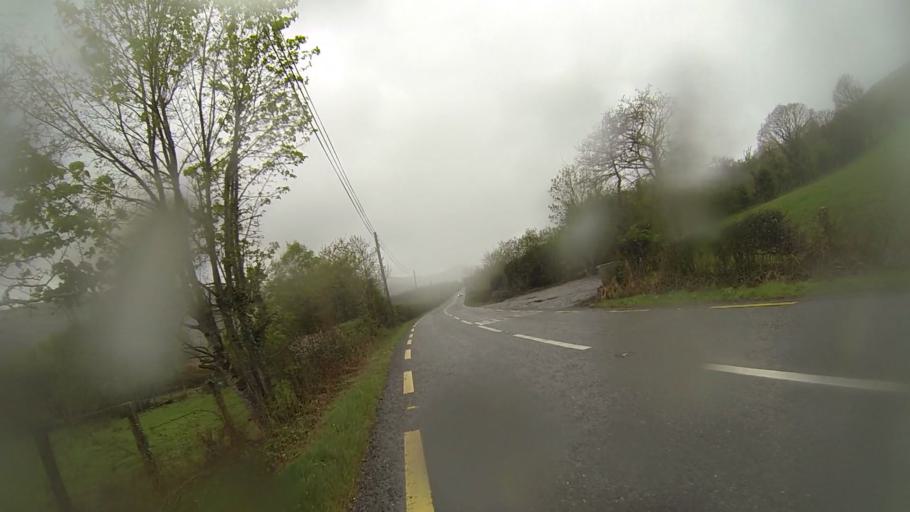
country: IE
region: Munster
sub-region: Ciarrai
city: Kenmare
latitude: 51.8229
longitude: -9.5271
